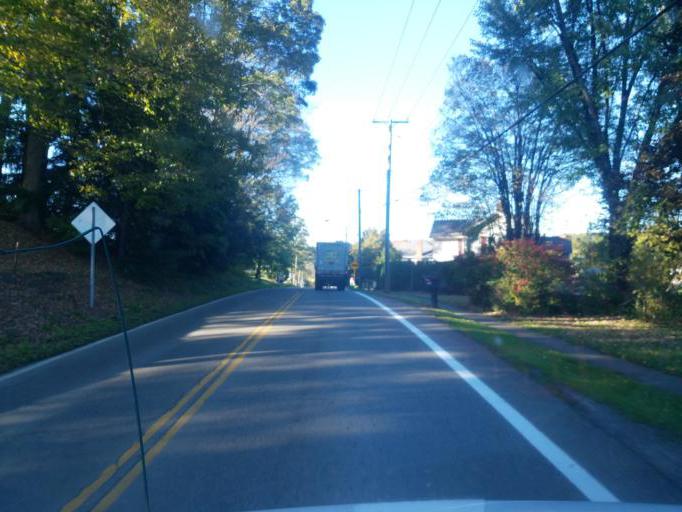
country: US
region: Ohio
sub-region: Columbiana County
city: New Waterford
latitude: 40.7904
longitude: -80.6257
